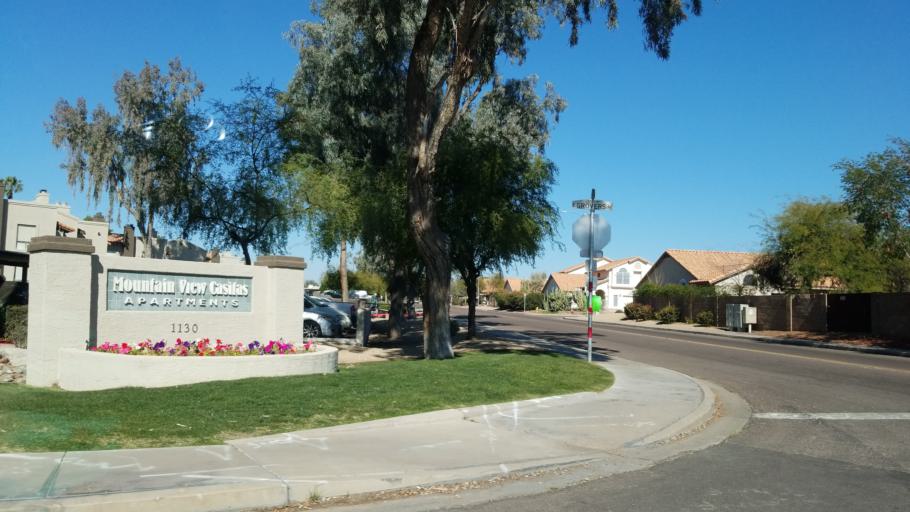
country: US
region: Arizona
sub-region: Maricopa County
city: Paradise Valley
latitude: 33.6476
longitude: -112.0570
